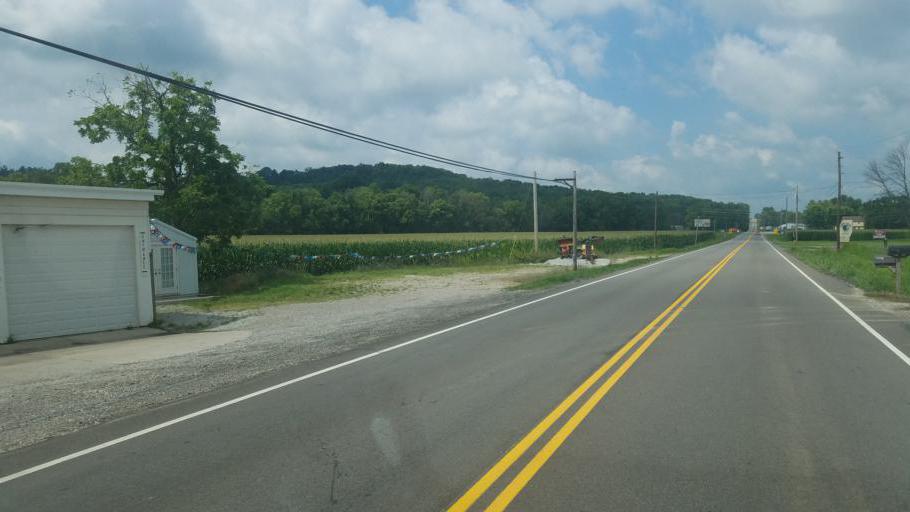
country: US
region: Ohio
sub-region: Fairfield County
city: Lancaster
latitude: 39.6847
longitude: -82.6723
